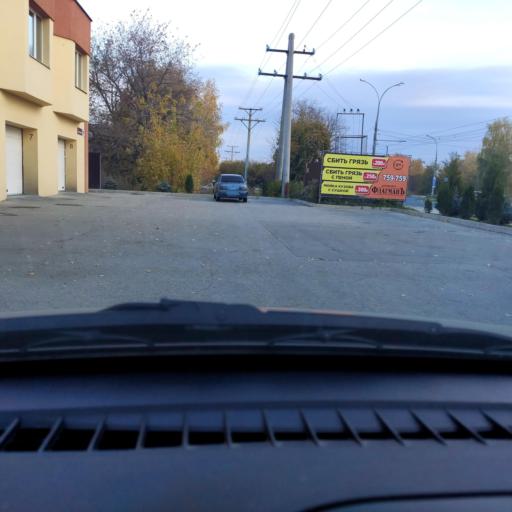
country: RU
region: Samara
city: Tol'yatti
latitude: 53.5428
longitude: 49.3004
